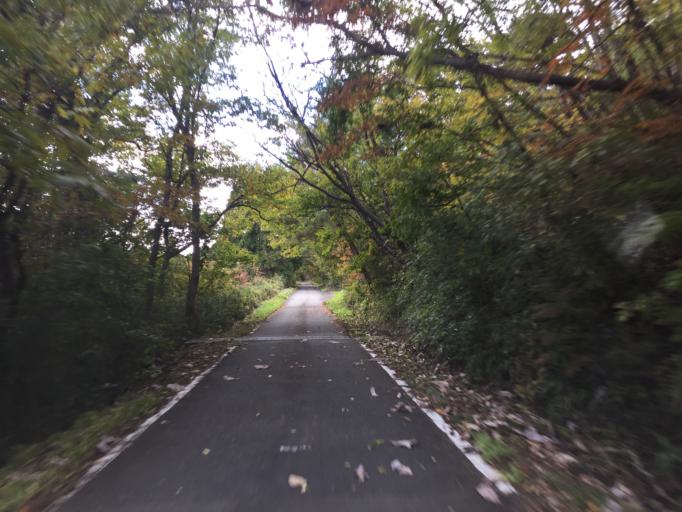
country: JP
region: Fukushima
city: Nihommatsu
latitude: 37.6757
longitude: 140.3932
